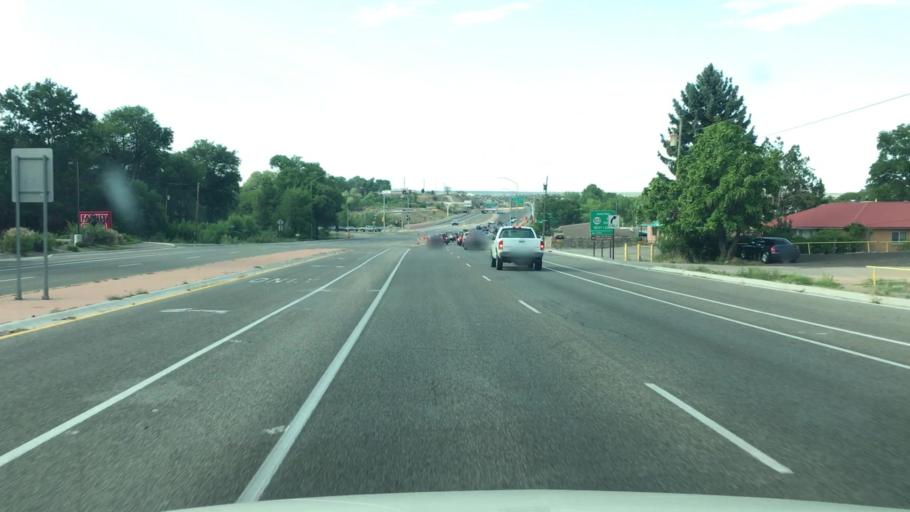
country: US
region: New Mexico
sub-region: Santa Fe County
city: Pojoaque
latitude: 35.8997
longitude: -106.0205
